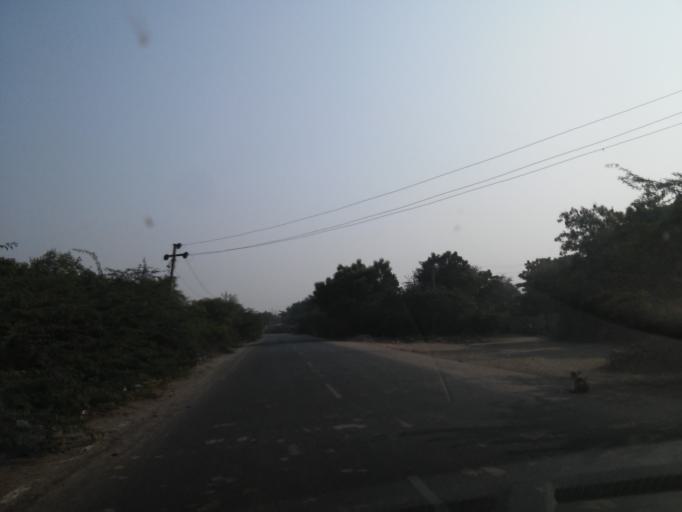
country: IN
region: Gujarat
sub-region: Kachchh
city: Mundra
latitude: 22.8334
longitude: 69.6517
